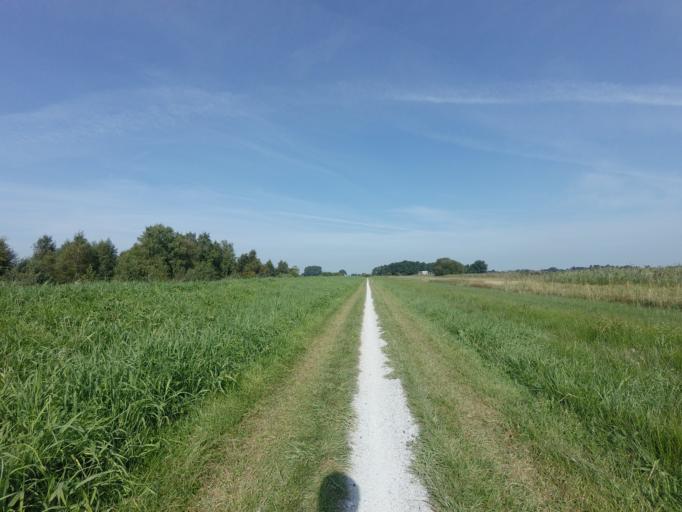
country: NL
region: Overijssel
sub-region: Gemeente Steenwijkerland
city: Oldemarkt
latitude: 52.8543
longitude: 5.9174
